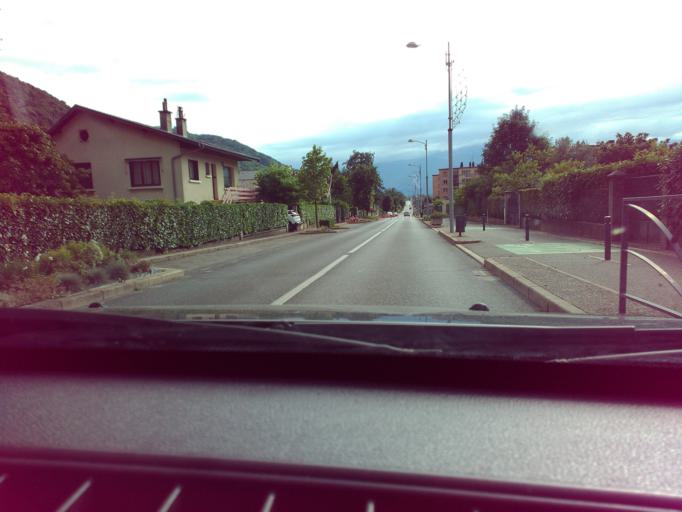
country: FR
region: Rhone-Alpes
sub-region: Departement de l'Isere
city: Domene
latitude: 45.1976
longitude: 5.8325
